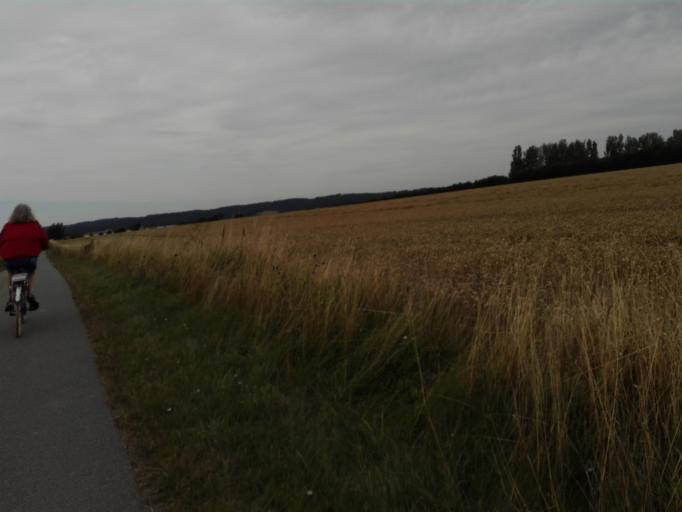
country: DK
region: Central Jutland
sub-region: Odder Kommune
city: Odder
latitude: 55.8583
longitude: 10.0628
